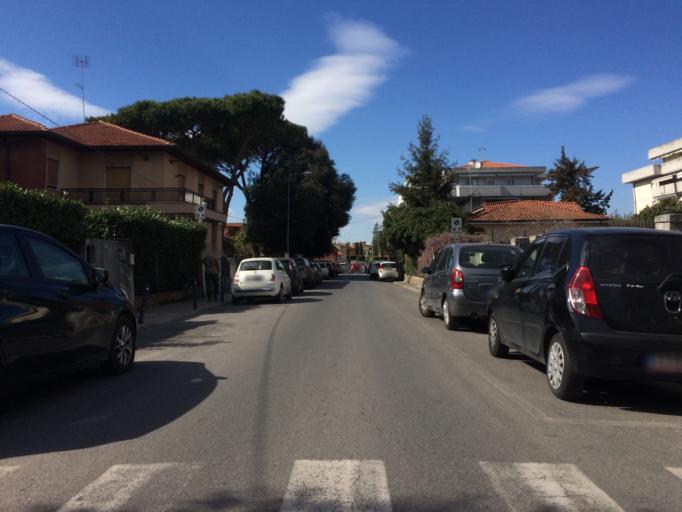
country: IT
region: Tuscany
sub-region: Provincia di Massa-Carrara
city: Carrara
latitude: 44.0513
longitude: 10.0568
